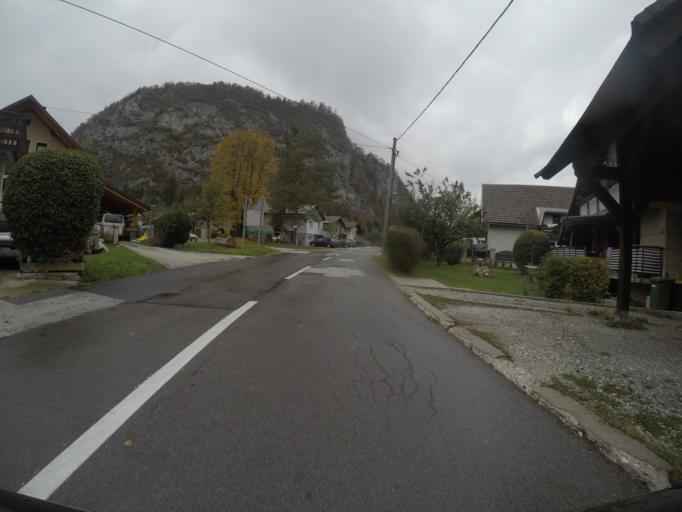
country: SI
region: Kranjska Gora
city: Mojstrana
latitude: 46.4610
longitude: 13.9370
